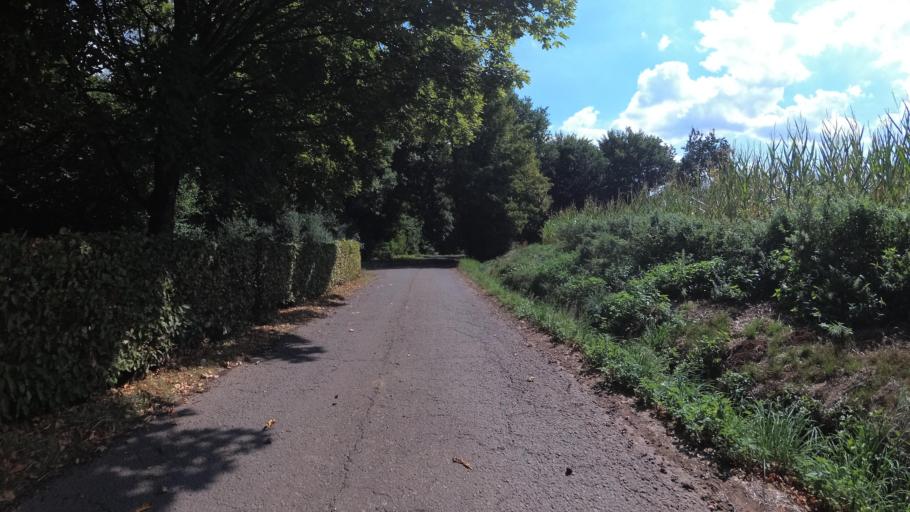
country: DE
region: Saarland
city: Mainzweiler
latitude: 49.4084
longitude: 7.1008
